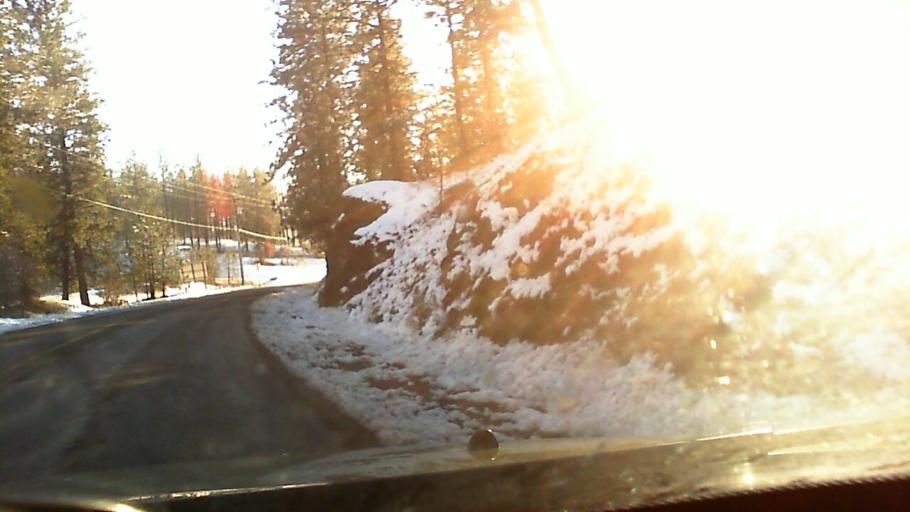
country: US
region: Washington
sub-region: Spokane County
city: Trentwood
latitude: 47.7238
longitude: -117.2126
